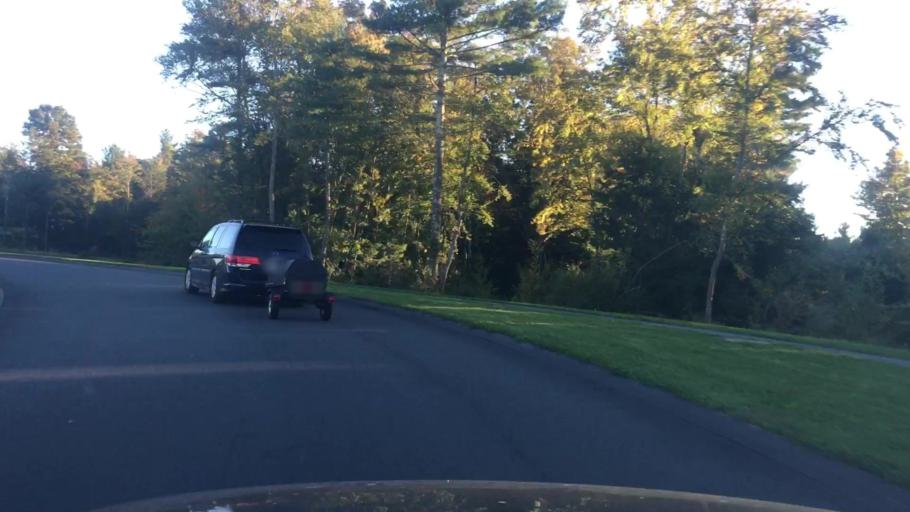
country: US
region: Massachusetts
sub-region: Worcester County
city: Charlton
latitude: 42.1372
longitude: -72.0138
